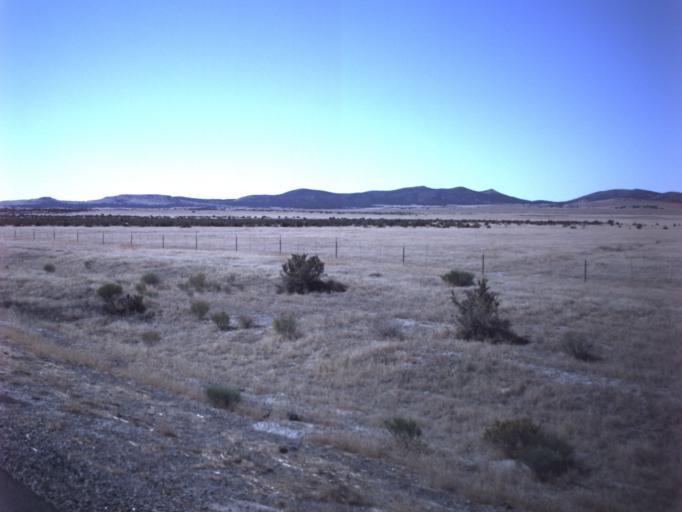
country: US
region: Utah
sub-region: Tooele County
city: Grantsville
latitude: 40.2999
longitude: -112.7428
